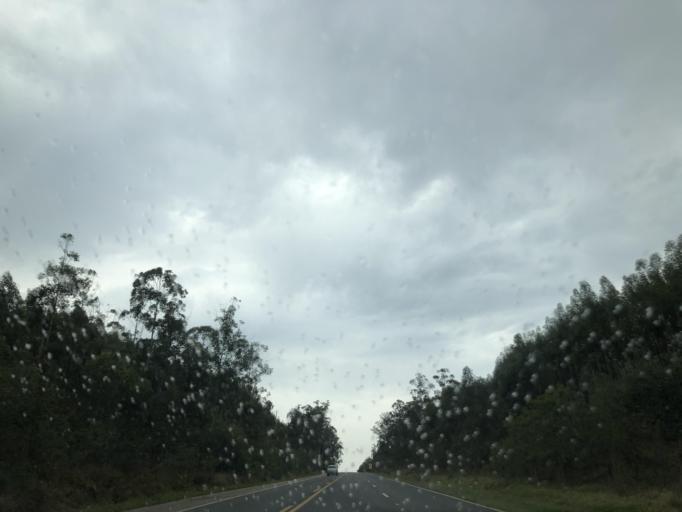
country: BR
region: Sao Paulo
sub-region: Salto De Pirapora
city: Salto de Pirapora
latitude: -23.6762
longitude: -47.6033
